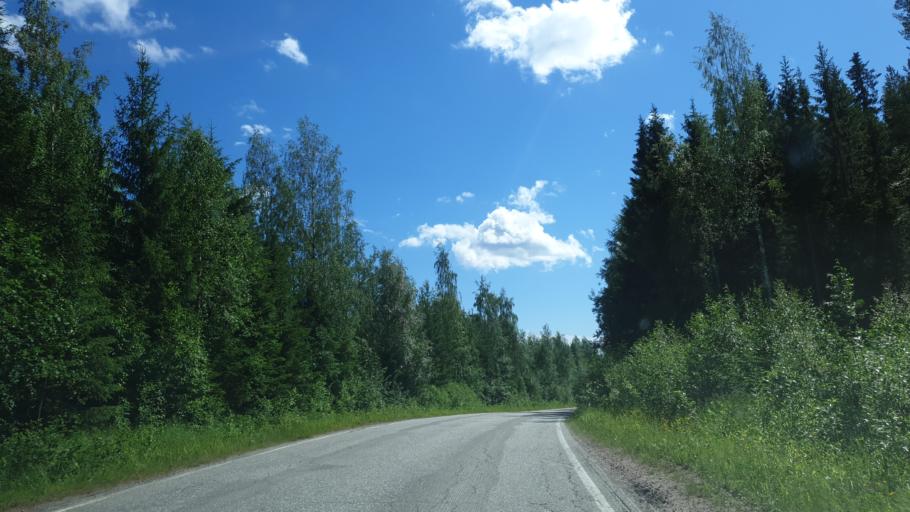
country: FI
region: Northern Savo
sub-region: Koillis-Savo
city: Kaavi
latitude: 63.0001
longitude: 28.5025
